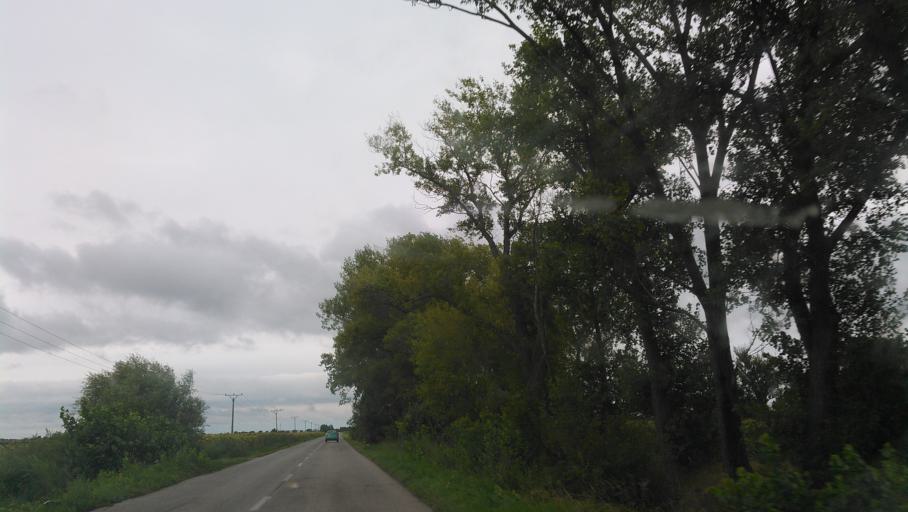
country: SK
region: Trnavsky
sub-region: Okres Dunajska Streda
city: Velky Meder
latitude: 47.8929
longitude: 17.8371
